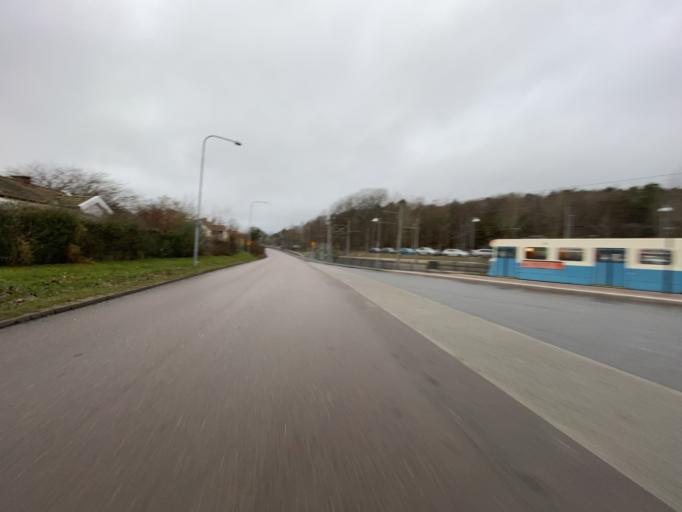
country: SE
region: Vaestra Goetaland
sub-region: Goteborg
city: Eriksbo
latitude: 57.7225
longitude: 12.0470
